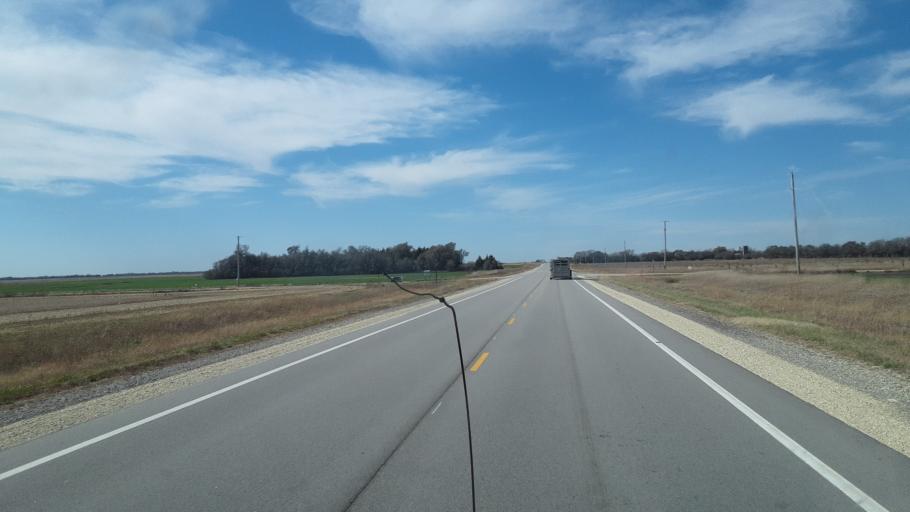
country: US
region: Kansas
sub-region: Marion County
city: Hillsboro
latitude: 38.3771
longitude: -97.3887
